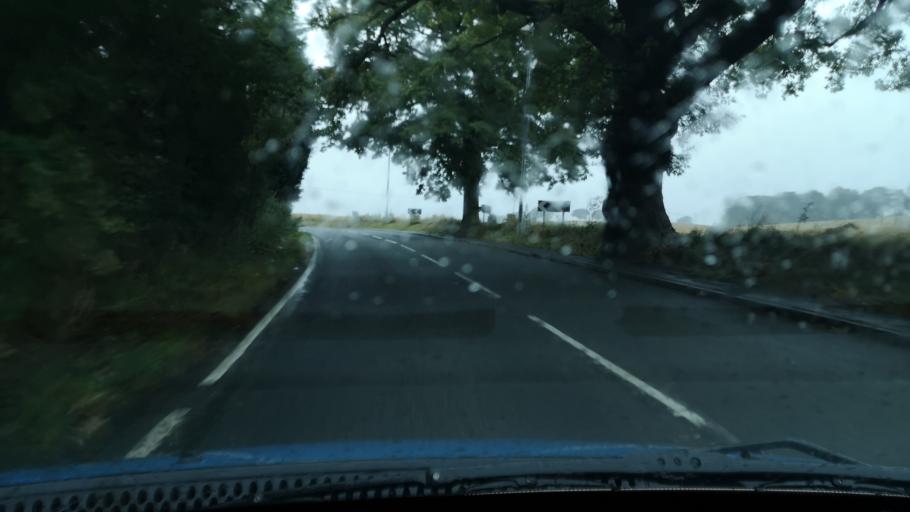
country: GB
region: England
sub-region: City and Borough of Wakefield
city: Low Ackworth
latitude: 53.6604
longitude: -1.3408
